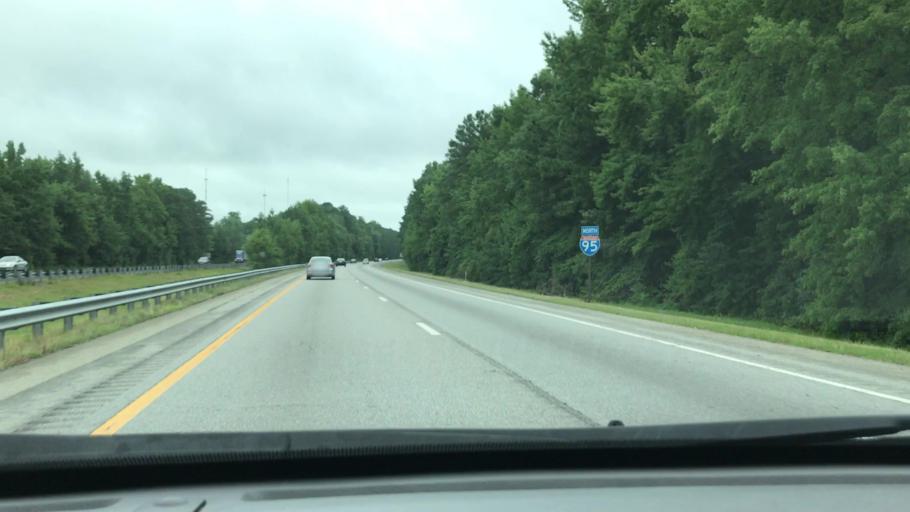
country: US
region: North Carolina
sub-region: Northampton County
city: Gaston
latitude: 36.4739
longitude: -77.6090
